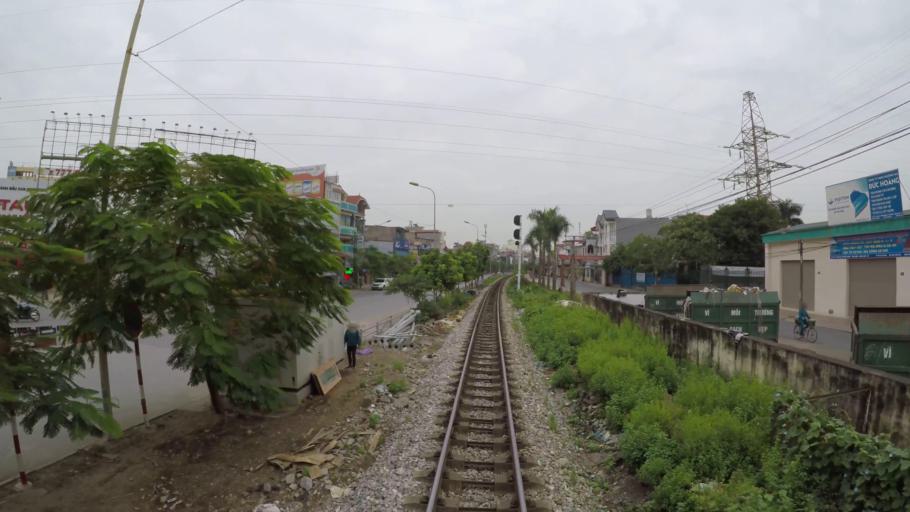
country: VN
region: Hai Phong
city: An Duong
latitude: 20.8751
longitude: 106.6384
